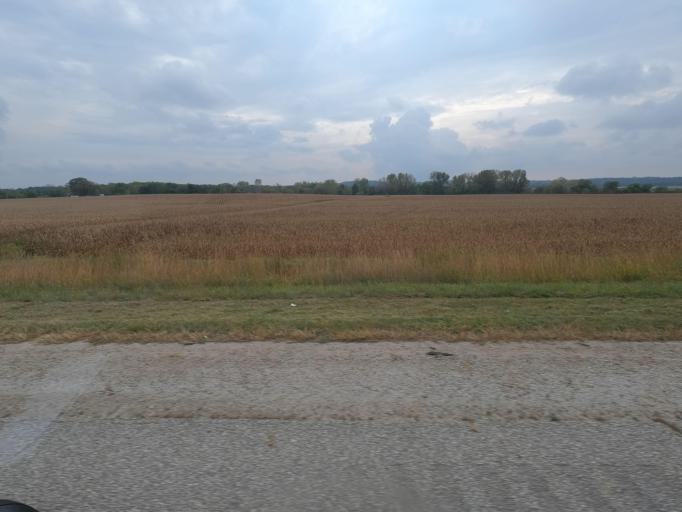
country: US
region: Iowa
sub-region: Wapello County
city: Eddyville
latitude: 41.1361
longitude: -92.5855
